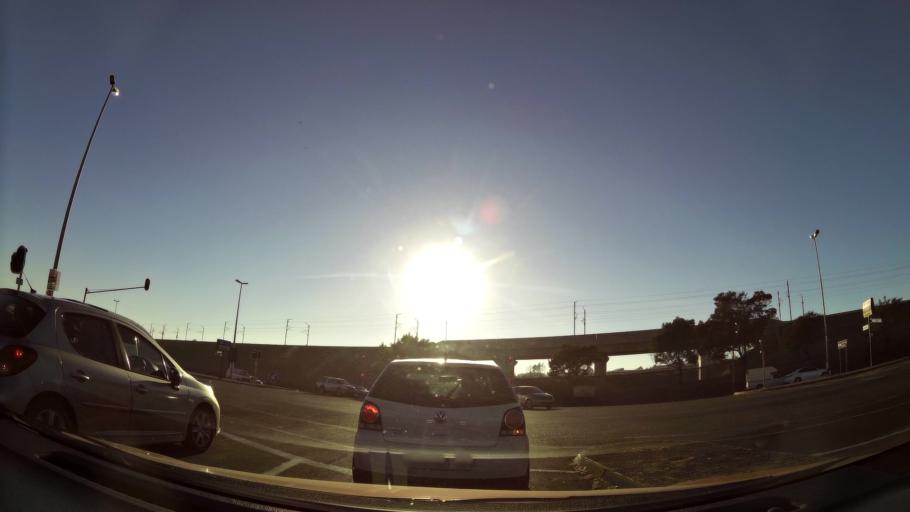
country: ZA
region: Gauteng
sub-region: City of Johannesburg Metropolitan Municipality
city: Midrand
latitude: -25.9882
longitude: 28.1317
